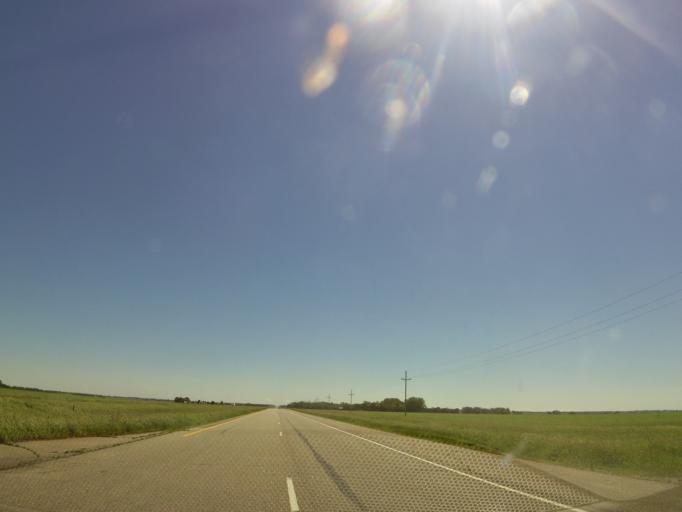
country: US
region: Minnesota
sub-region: Polk County
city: Crookston
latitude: 47.7603
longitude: -96.5144
